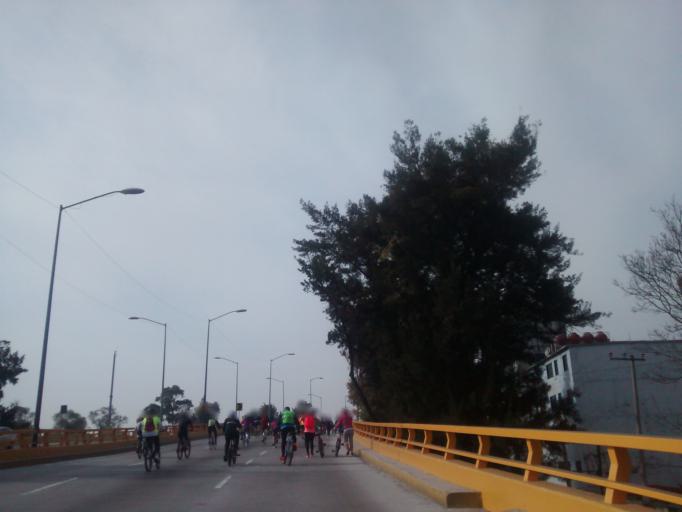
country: MX
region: Mexico City
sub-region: Iztacalco
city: Iztacalco
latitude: 19.3729
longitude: -99.1026
